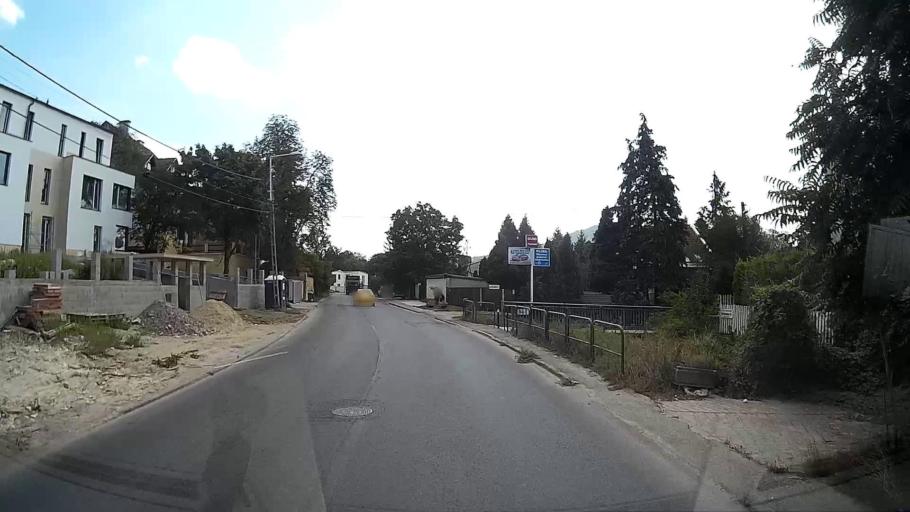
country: HU
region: Pest
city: Solymar
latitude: 47.5510
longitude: 18.9499
